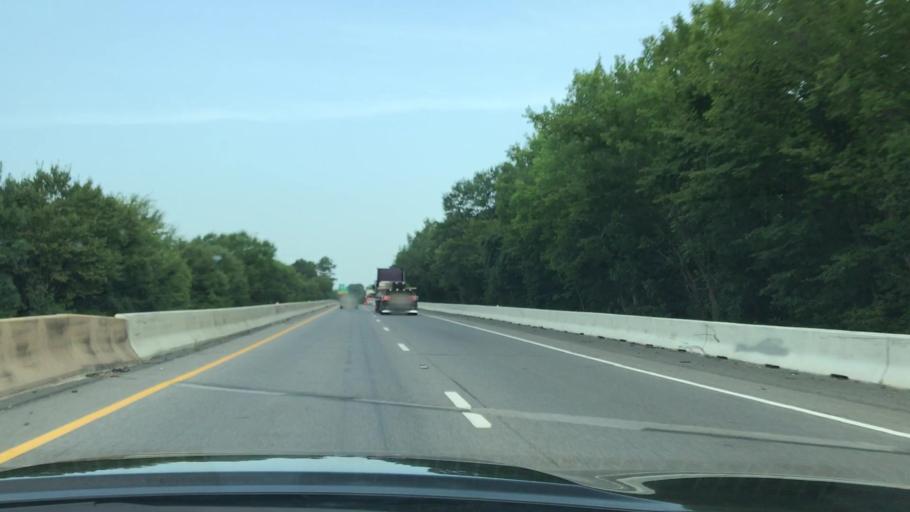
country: US
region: Texas
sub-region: Gregg County
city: Kilgore
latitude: 32.4352
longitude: -94.8206
